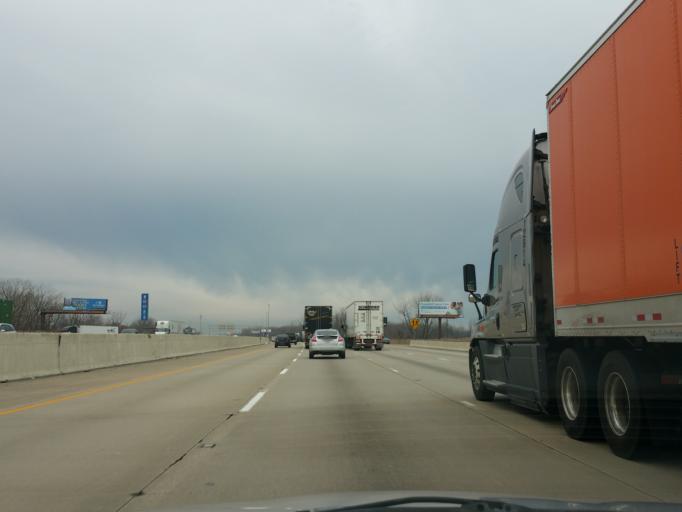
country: US
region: Indiana
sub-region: Lake County
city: Gary
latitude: 41.5693
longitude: -87.3573
